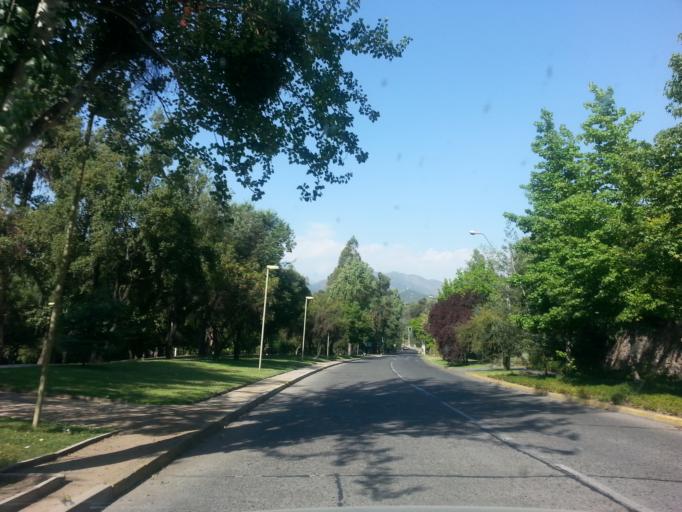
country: CL
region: Santiago Metropolitan
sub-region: Provincia de Santiago
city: Villa Presidente Frei, Nunoa, Santiago, Chile
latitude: -33.3868
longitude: -70.5226
